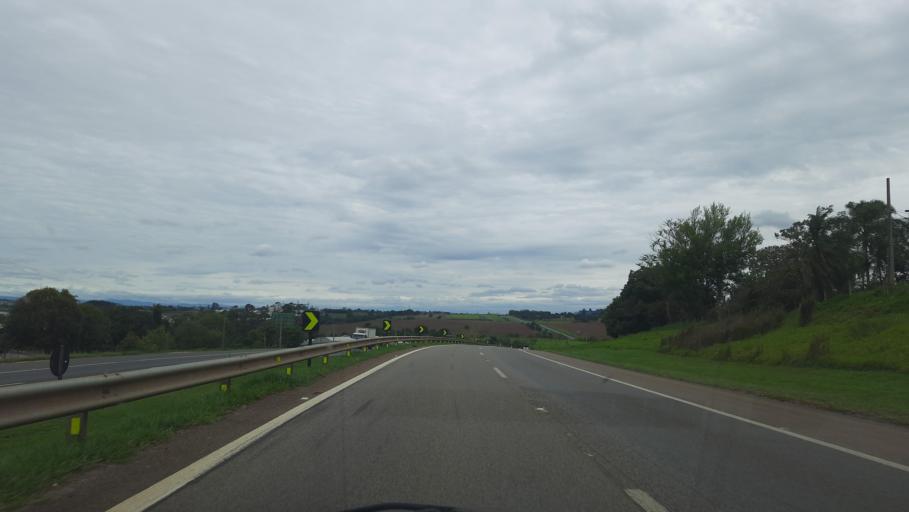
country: BR
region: Sao Paulo
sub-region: Moji-Guacu
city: Mogi-Gaucu
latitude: -22.2690
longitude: -46.9732
